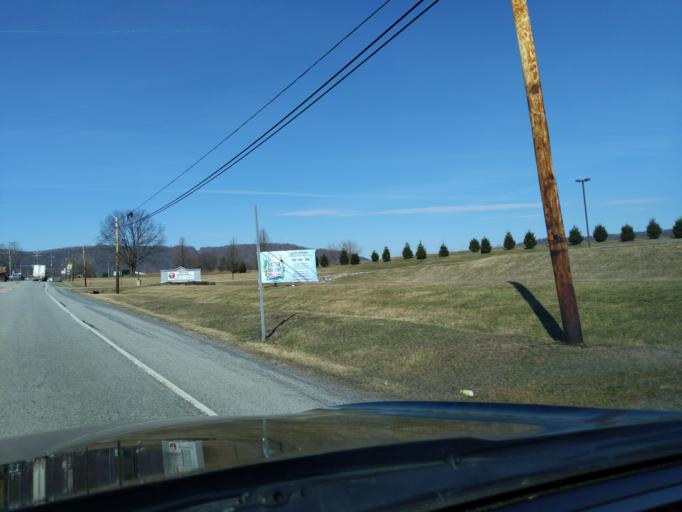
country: US
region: Pennsylvania
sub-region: Blair County
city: Roaring Spring
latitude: 40.3342
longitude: -78.3824
